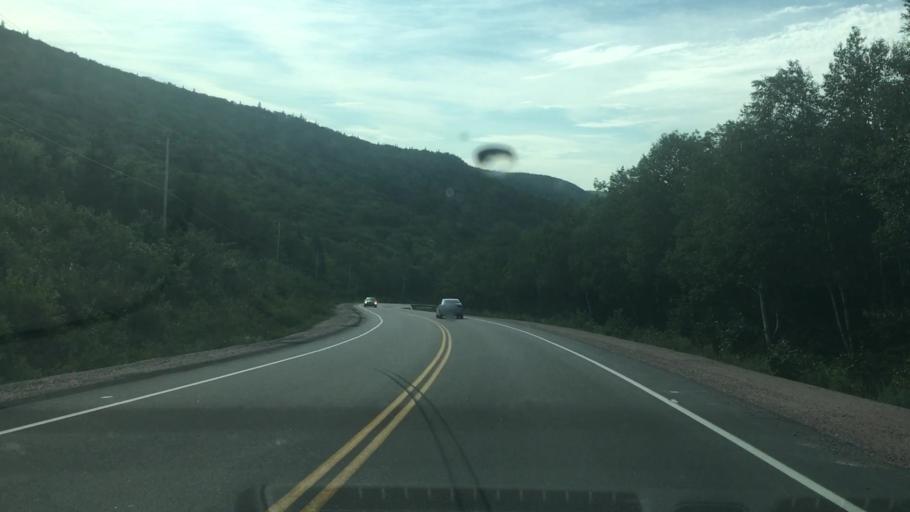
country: CA
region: Nova Scotia
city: Sydney Mines
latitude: 46.8555
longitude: -60.4500
